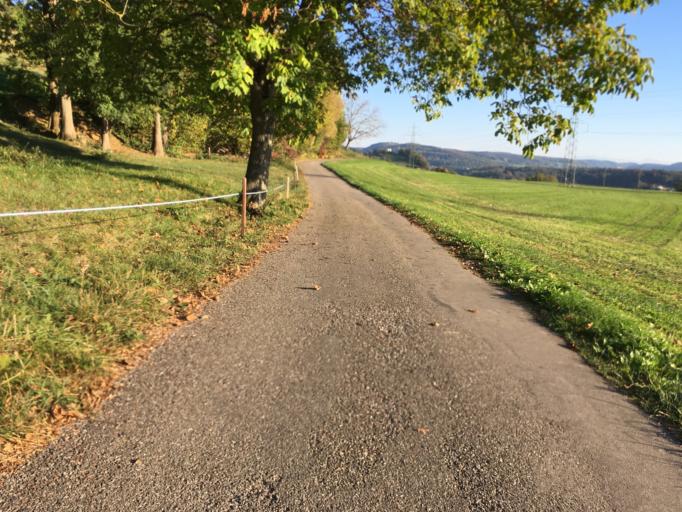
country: CH
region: Zurich
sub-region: Bezirk Buelach
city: Rorbas
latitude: 47.5434
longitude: 8.5722
